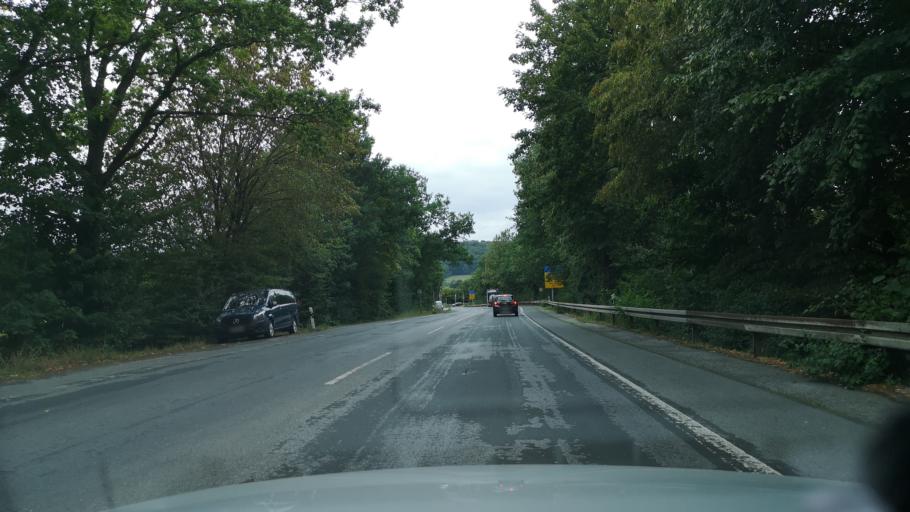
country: DE
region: North Rhine-Westphalia
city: Schwerte
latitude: 51.4102
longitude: 7.5165
